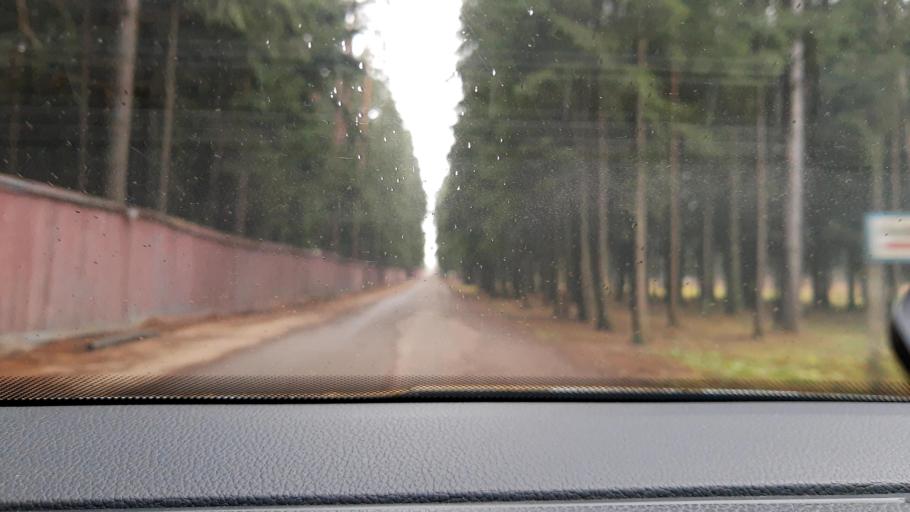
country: RU
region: Moskovskaya
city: Pushkino
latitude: 56.0109
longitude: 37.8895
